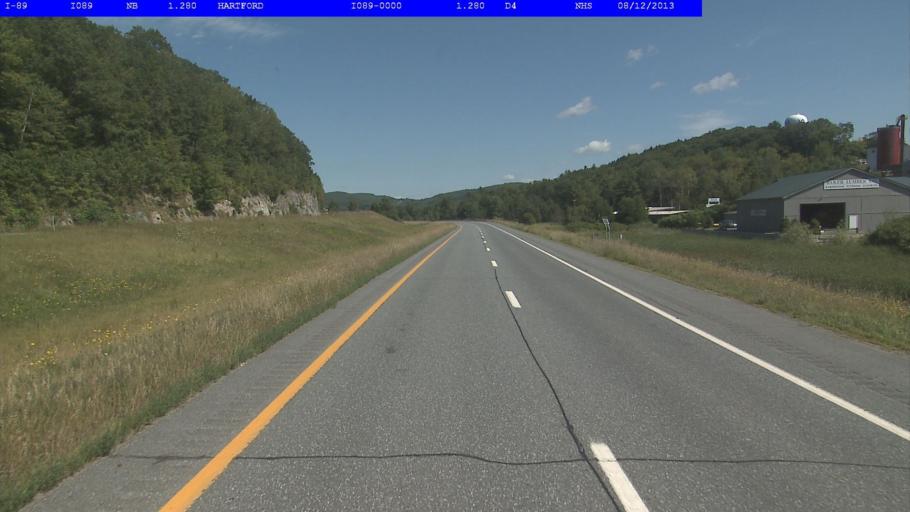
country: US
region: Vermont
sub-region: Windsor County
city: White River Junction
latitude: 43.6478
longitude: -72.3465
